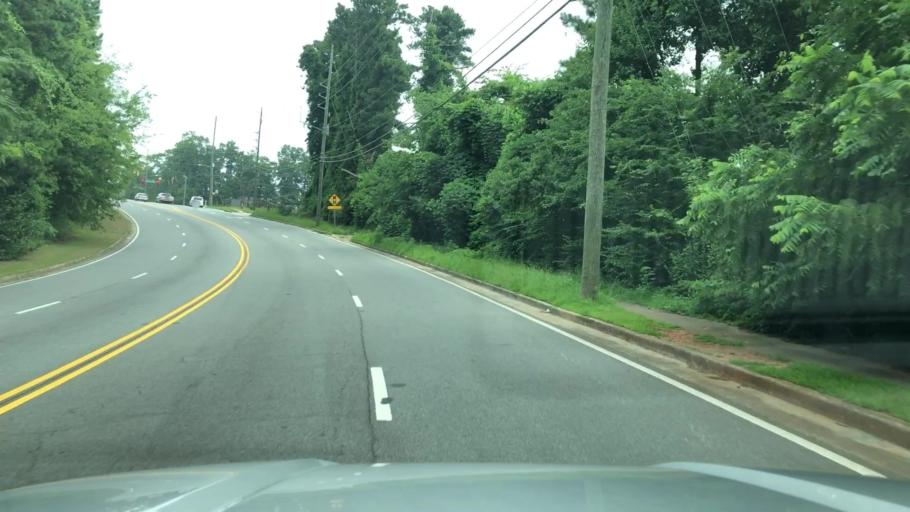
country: US
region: Georgia
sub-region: Cobb County
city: Mableton
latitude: 33.7770
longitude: -84.5761
